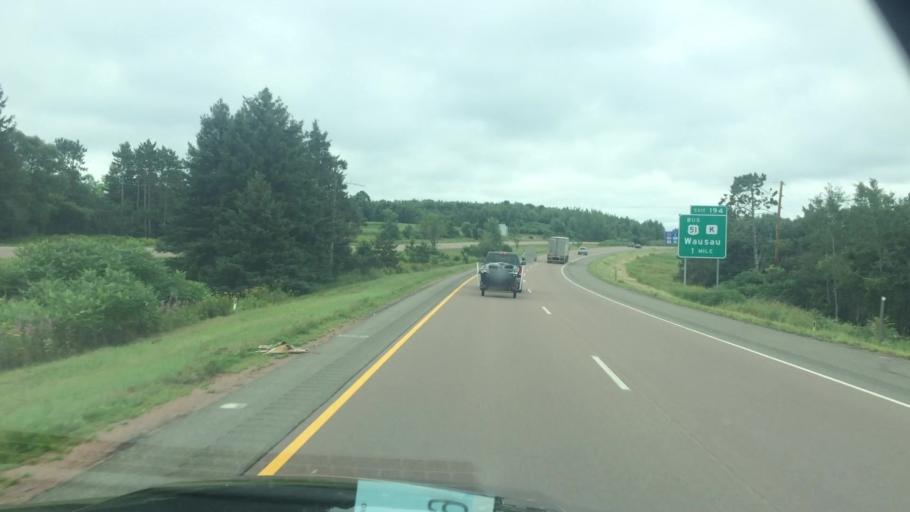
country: US
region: Wisconsin
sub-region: Marathon County
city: Wausau
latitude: 45.0108
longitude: -89.6626
